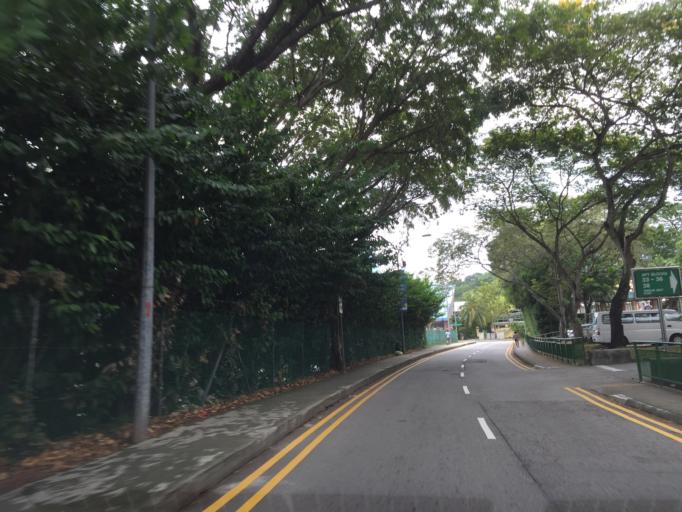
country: SG
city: Singapore
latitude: 1.2969
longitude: 103.7990
